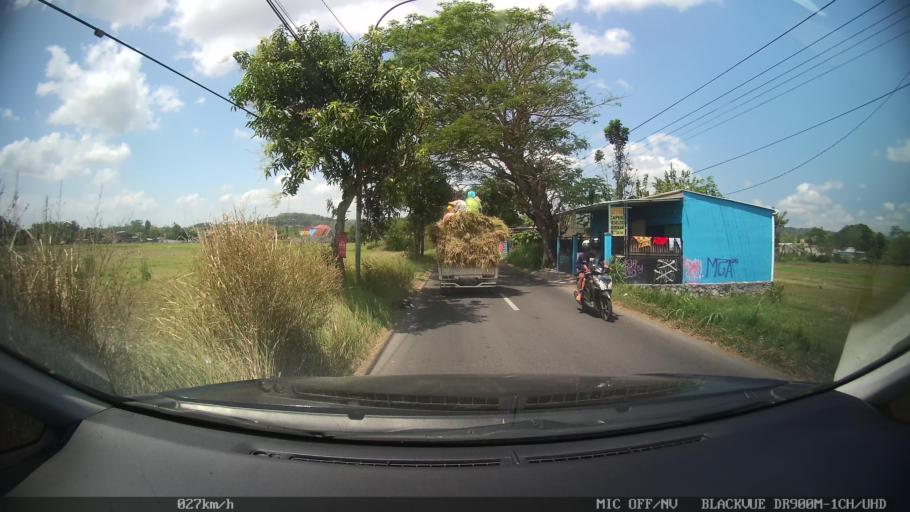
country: ID
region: Daerah Istimewa Yogyakarta
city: Sewon
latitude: -7.8983
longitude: 110.3814
